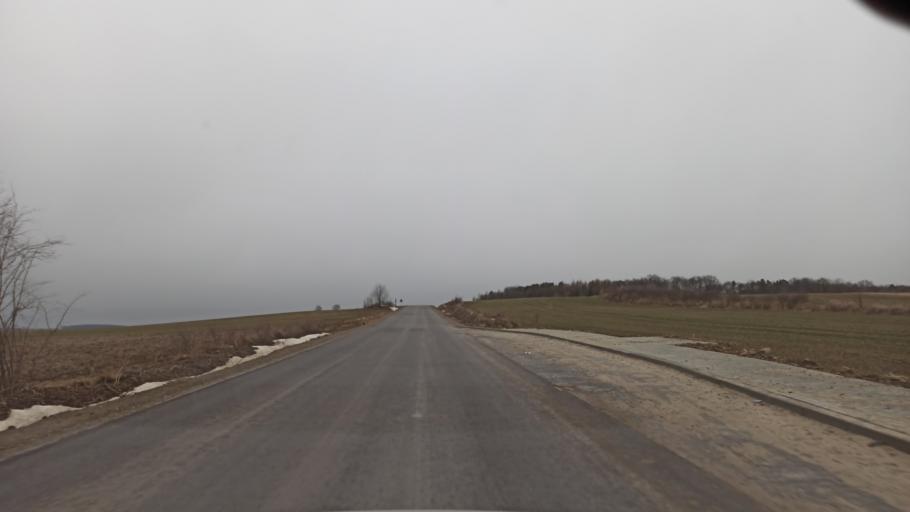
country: PL
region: Lublin Voivodeship
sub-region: Powiat lubelski
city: Wysokie
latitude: 50.9287
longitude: 22.6363
